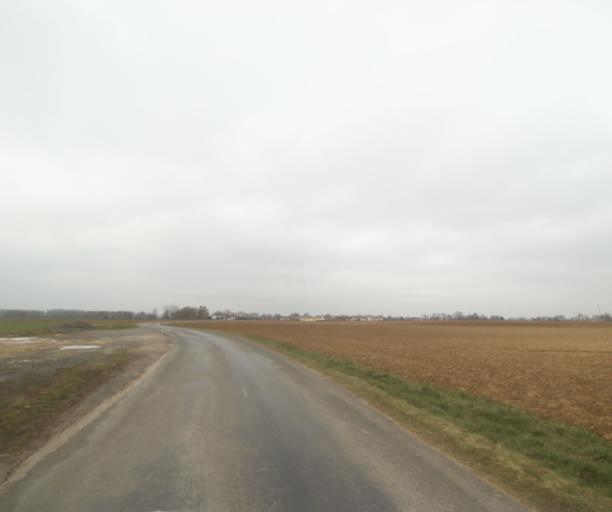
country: FR
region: Champagne-Ardenne
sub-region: Departement de la Marne
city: Pargny-sur-Saulx
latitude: 48.6890
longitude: 4.8119
